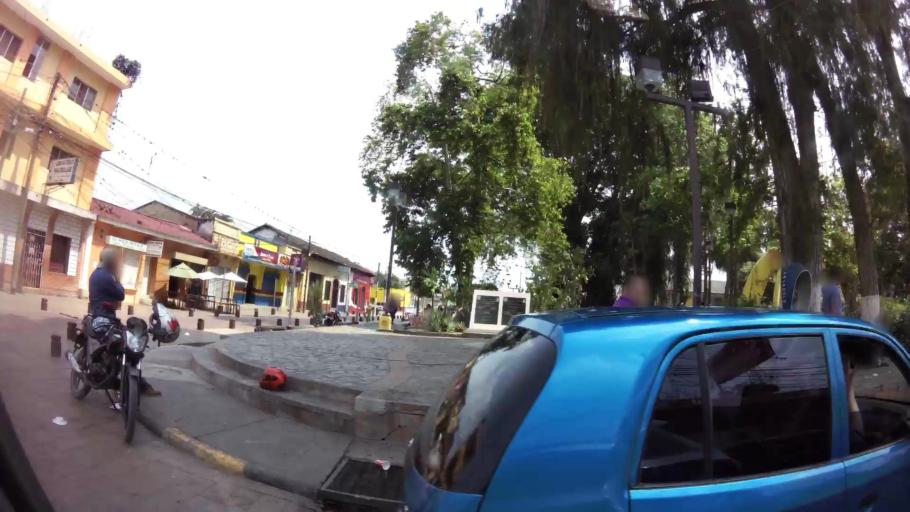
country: HN
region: Comayagua
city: Siguatepeque
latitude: 14.5963
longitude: -87.8287
